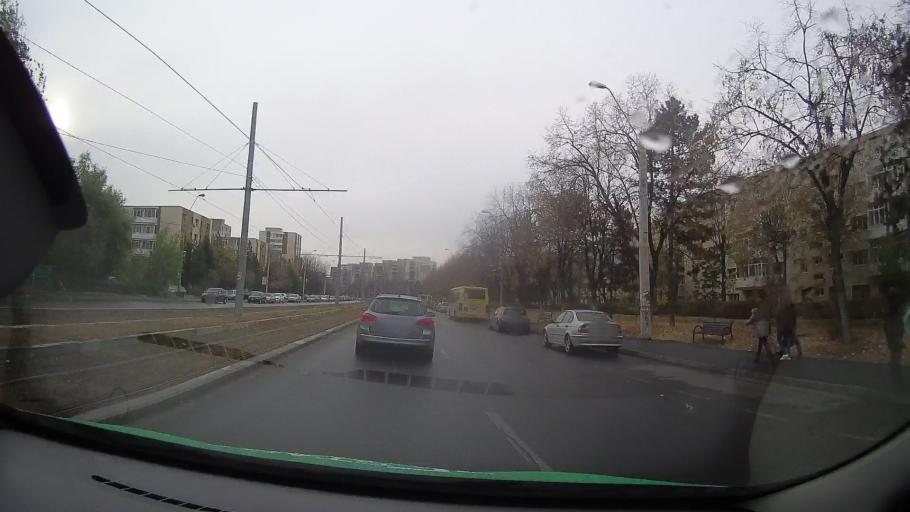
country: RO
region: Prahova
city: Ploiesti
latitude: 44.9338
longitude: 25.9893
